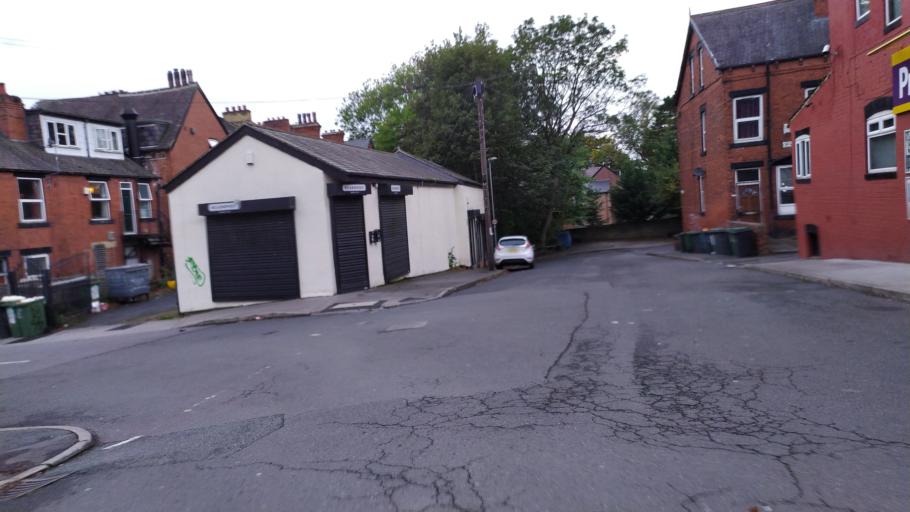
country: GB
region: England
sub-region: City and Borough of Leeds
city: Leeds
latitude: 53.8149
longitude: -1.5738
